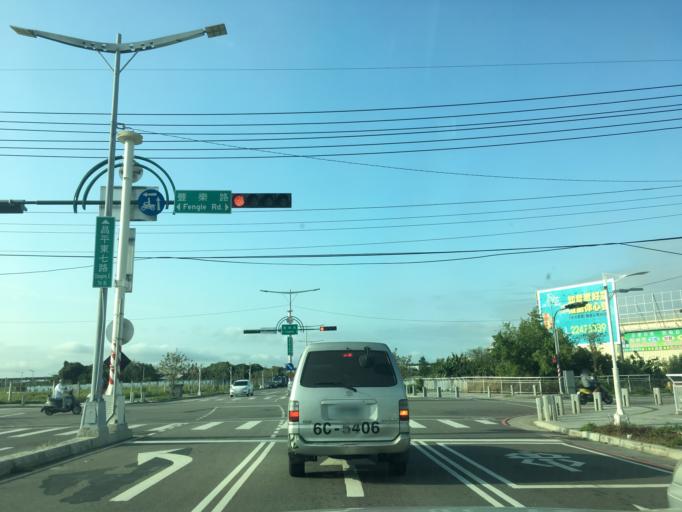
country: TW
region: Taiwan
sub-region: Taichung City
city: Taichung
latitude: 24.1925
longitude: 120.6934
